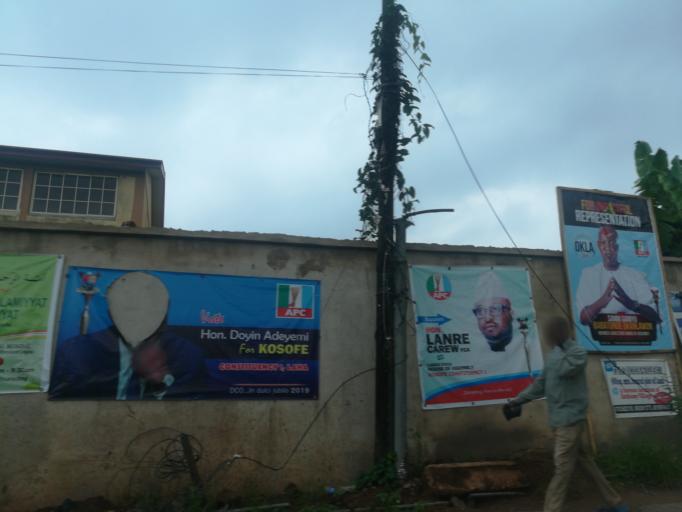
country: NG
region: Lagos
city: Ojota
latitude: 6.5686
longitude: 3.3688
